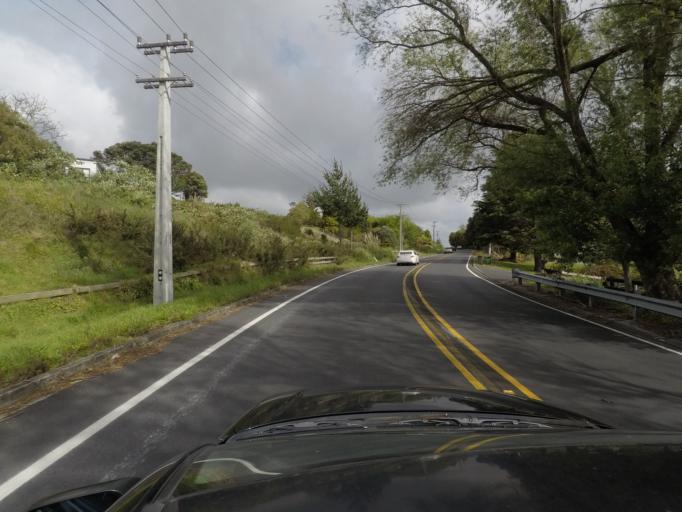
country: NZ
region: Auckland
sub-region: Auckland
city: Pakuranga
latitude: -36.9303
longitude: 174.9376
